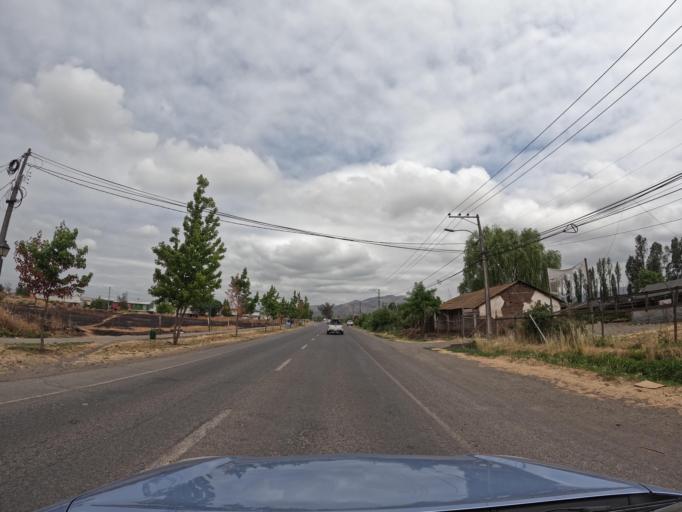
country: CL
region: Maule
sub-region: Provincia de Curico
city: Teno
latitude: -34.8668
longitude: -71.1695
